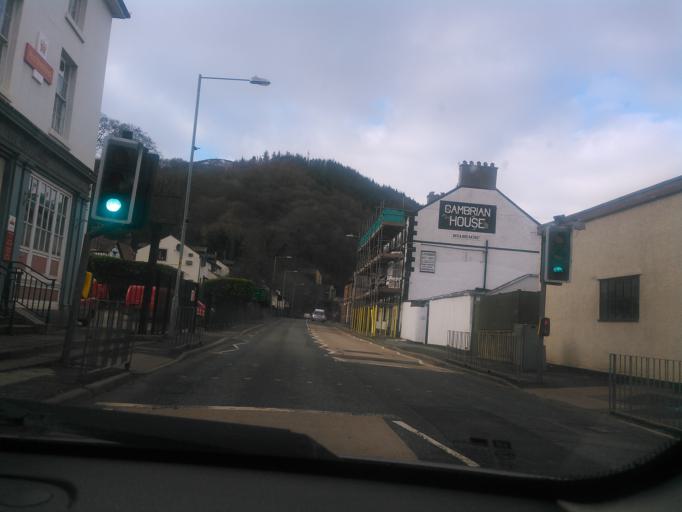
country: GB
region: Wales
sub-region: Denbighshire
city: Llangollen
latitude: 52.9690
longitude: -3.1720
